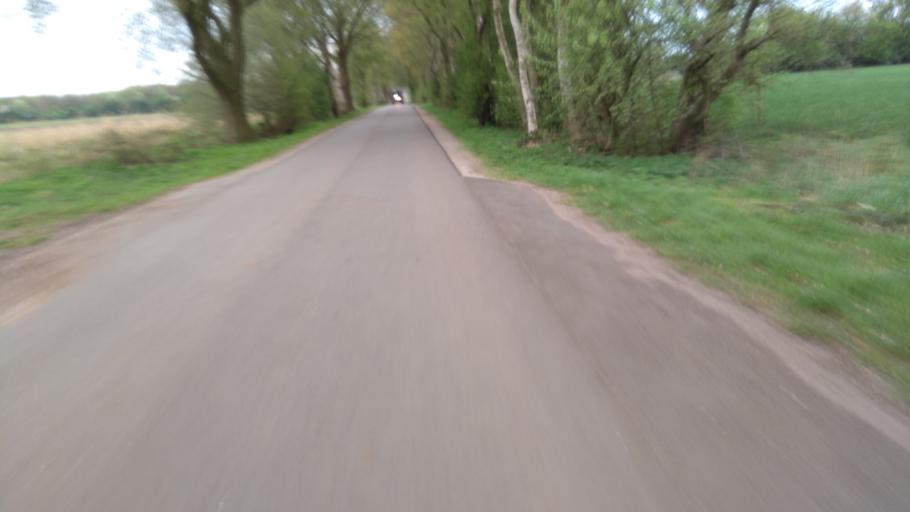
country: DE
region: Lower Saxony
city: Bliedersdorf
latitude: 53.4419
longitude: 9.5583
